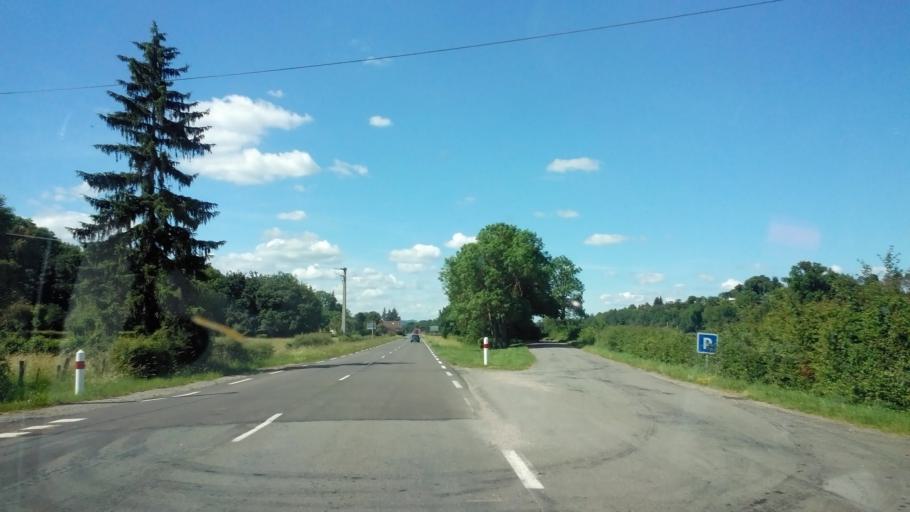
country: FR
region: Bourgogne
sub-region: Departement de Saone-et-Loire
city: Saint-Gengoux-le-National
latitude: 46.5292
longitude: 4.6860
